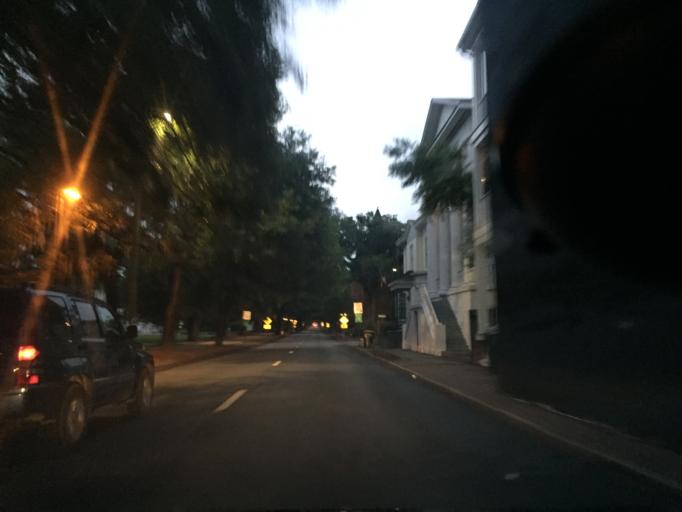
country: US
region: Georgia
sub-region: Chatham County
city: Savannah
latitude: 32.0661
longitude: -81.0955
